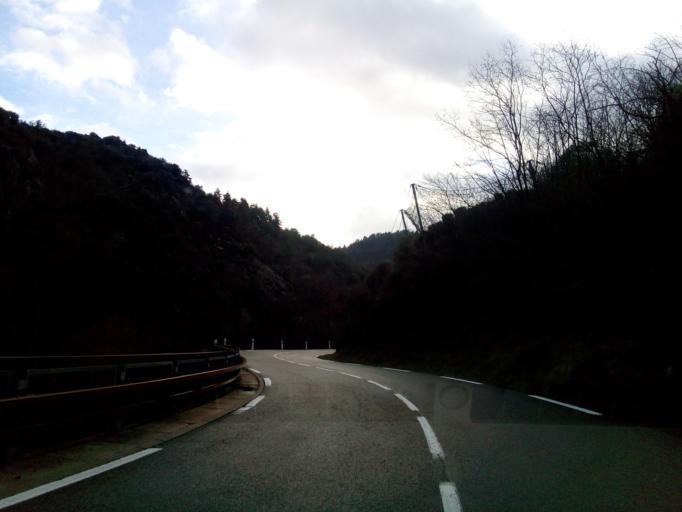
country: FR
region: Rhone-Alpes
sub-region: Departement de l'Ardeche
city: Saint-Sauveur-de-Montagut
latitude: 44.8683
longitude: 4.5541
